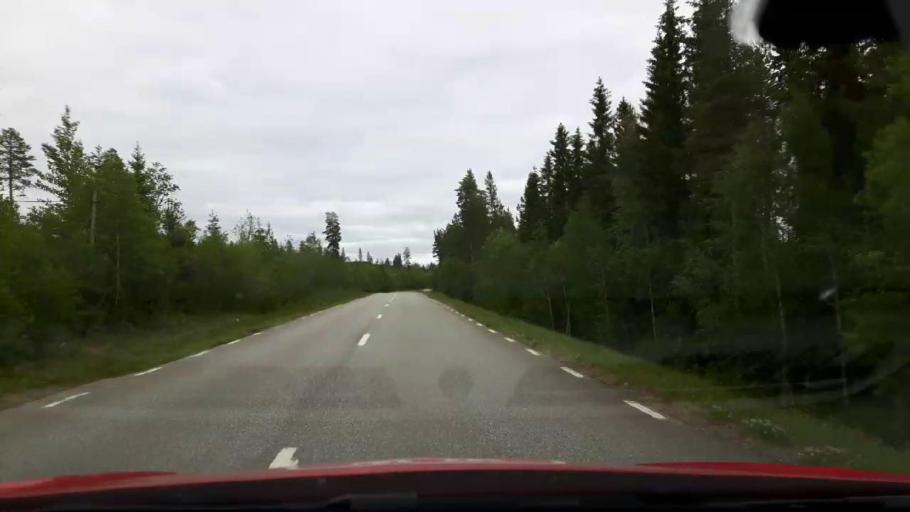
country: SE
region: Jaemtland
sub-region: Stroemsunds Kommun
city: Stroemsund
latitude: 63.3780
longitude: 15.6903
